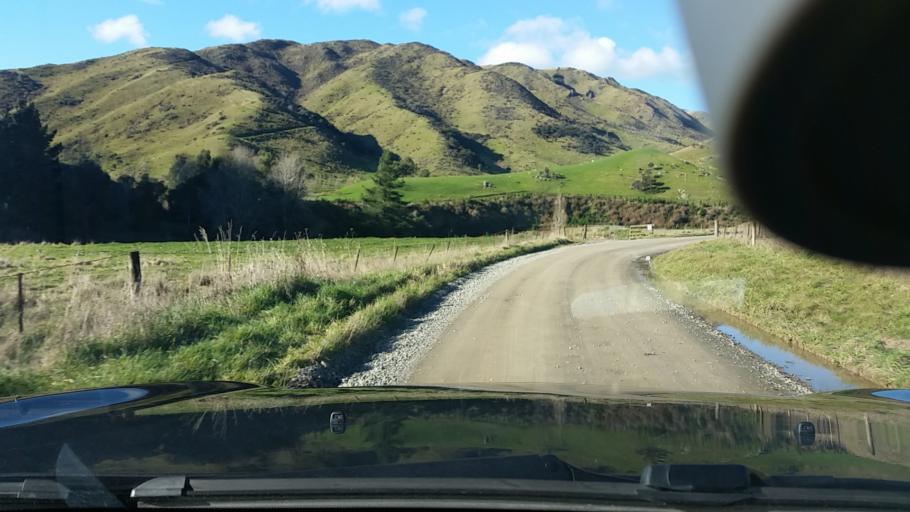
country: NZ
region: Marlborough
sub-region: Marlborough District
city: Blenheim
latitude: -41.6030
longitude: 173.9706
